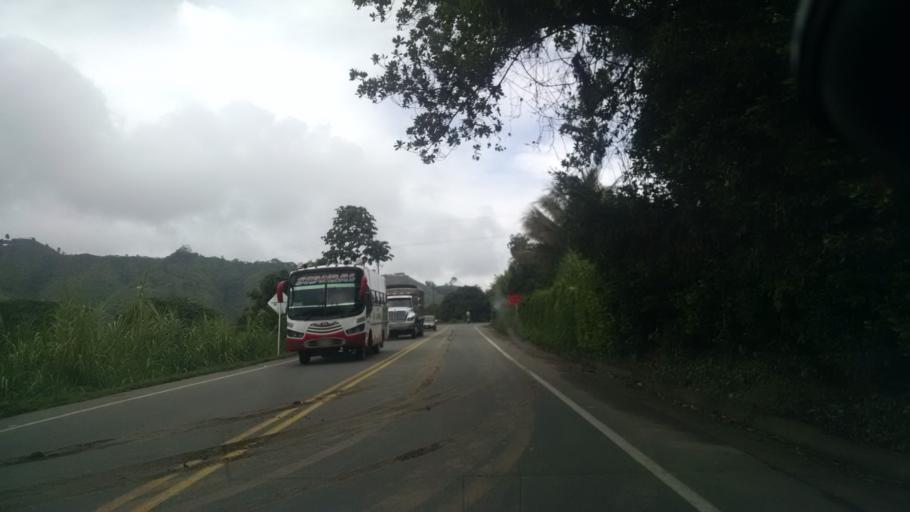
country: CO
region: Caldas
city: Palestina
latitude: 5.0689
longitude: -75.6366
